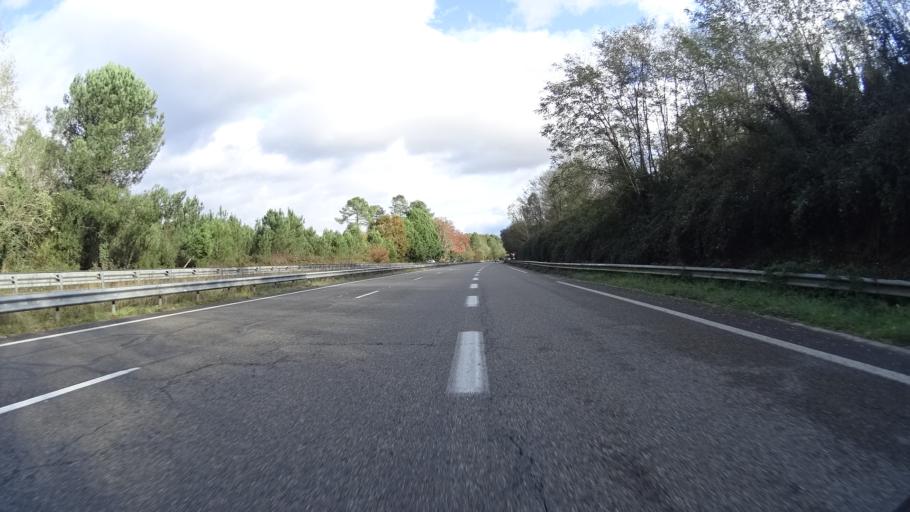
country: FR
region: Aquitaine
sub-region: Departement des Landes
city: Saint-Paul-les-Dax
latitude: 43.7445
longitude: -1.0521
